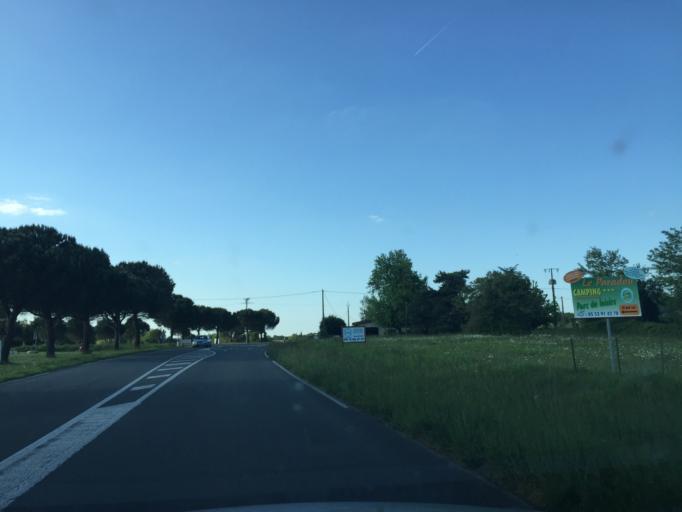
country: FR
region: Aquitaine
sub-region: Departement de la Dordogne
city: La Roche-Chalais
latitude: 45.1893
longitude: 0.0294
